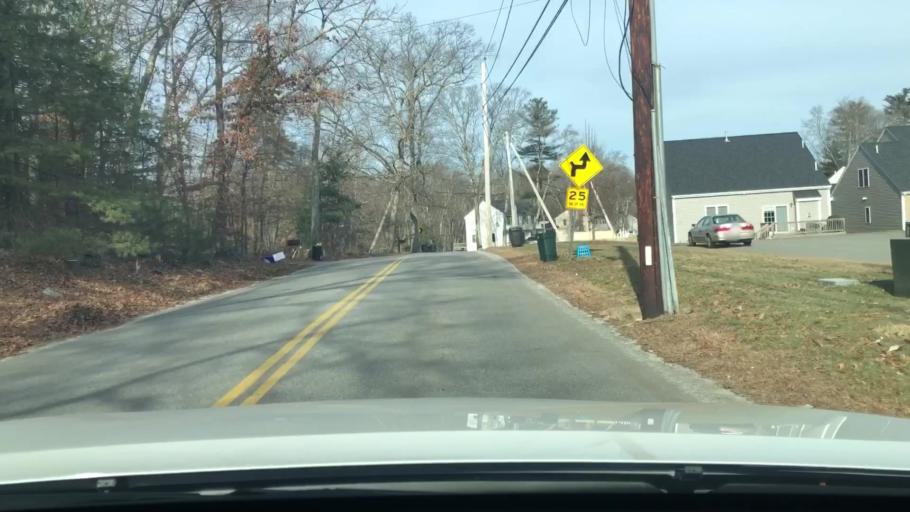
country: US
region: Massachusetts
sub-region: Worcester County
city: Milford
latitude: 42.1225
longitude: -71.4956
